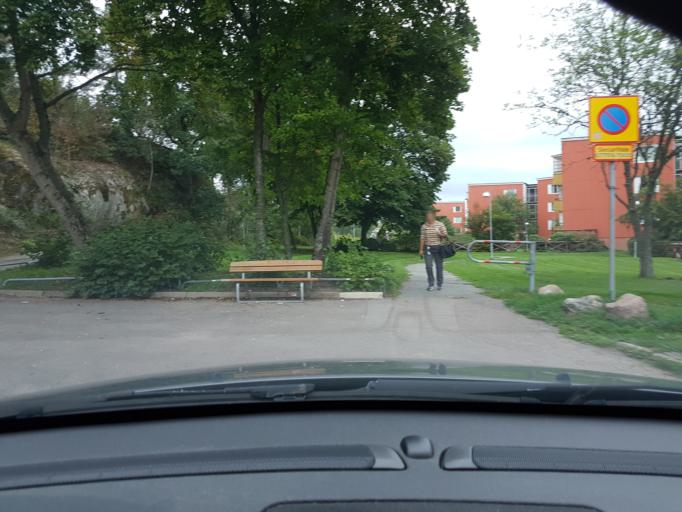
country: SE
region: Vaestra Goetaland
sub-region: Ale Kommun
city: Nodinge-Nol
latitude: 57.9139
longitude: 12.0662
